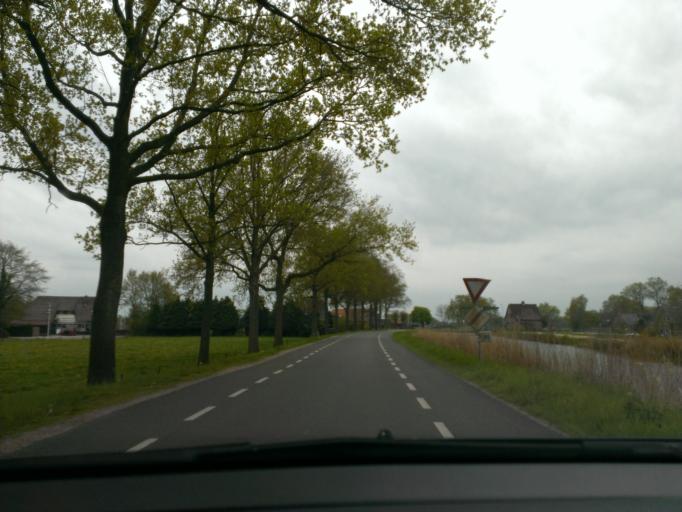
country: NL
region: Gelderland
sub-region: Gemeente Epe
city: Oene
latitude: 52.3471
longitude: 6.0244
